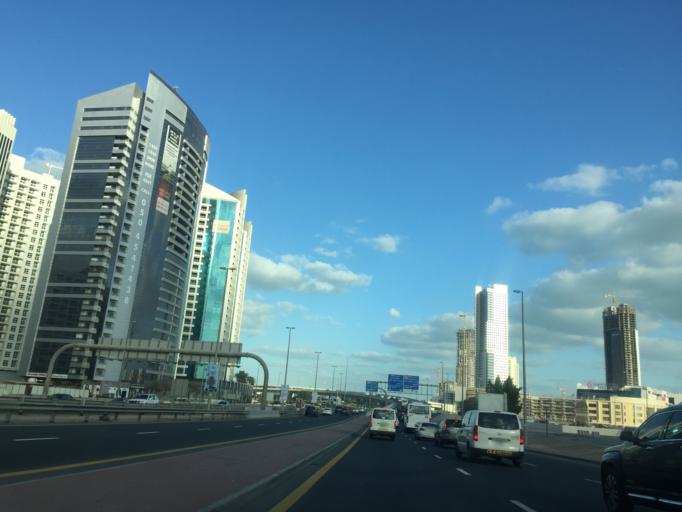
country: AE
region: Dubai
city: Dubai
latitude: 25.0999
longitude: 55.1807
